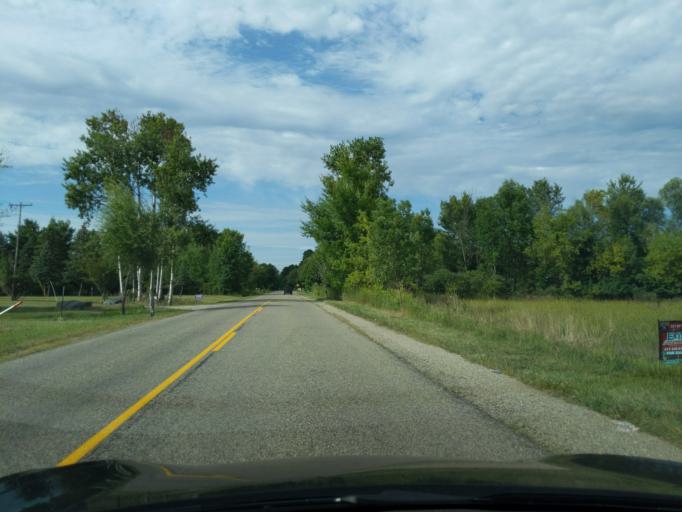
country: US
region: Michigan
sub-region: Eaton County
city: Dimondale
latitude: 42.6788
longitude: -84.6228
